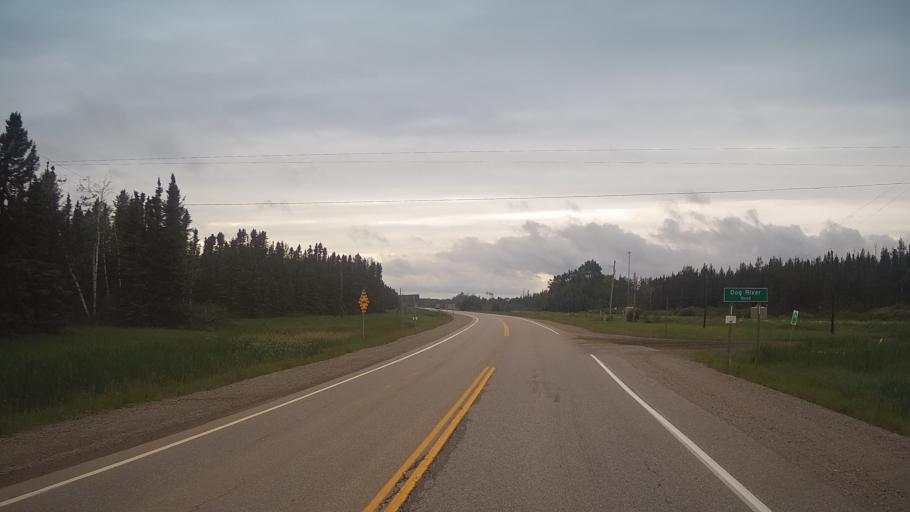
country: CA
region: Ontario
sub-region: Thunder Bay District
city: Thunder Bay
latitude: 48.8907
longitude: -90.0075
